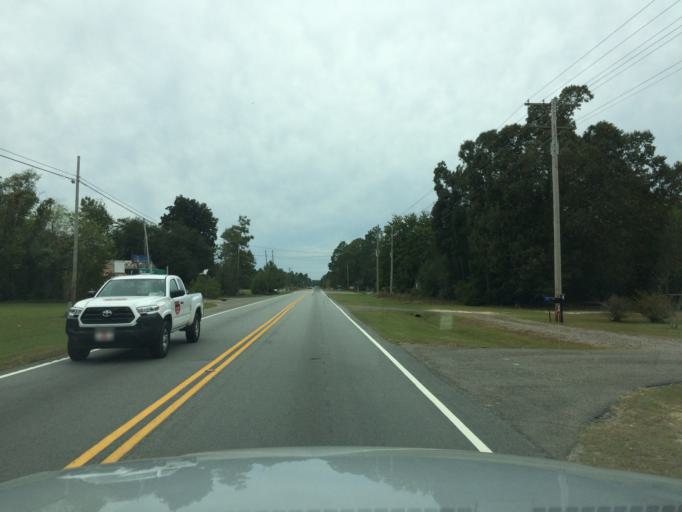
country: US
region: South Carolina
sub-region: Aiken County
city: New Ellenton
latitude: 33.3927
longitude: -81.7215
